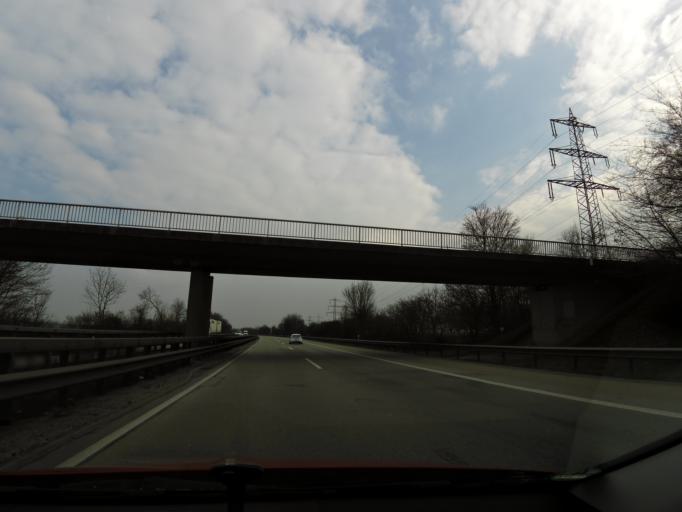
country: DE
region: Rheinland-Pfalz
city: Armsheim
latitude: 49.7981
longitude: 8.0624
